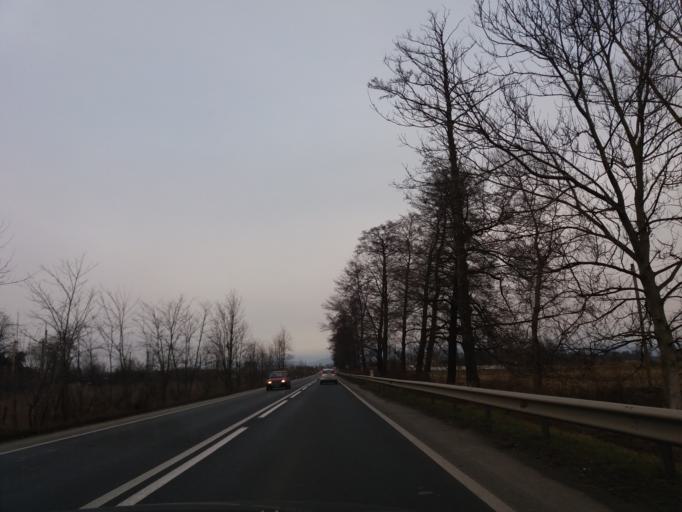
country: RO
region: Hunedoara
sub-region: Comuna Bacia
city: Bacia
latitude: 45.7912
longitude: 23.0012
